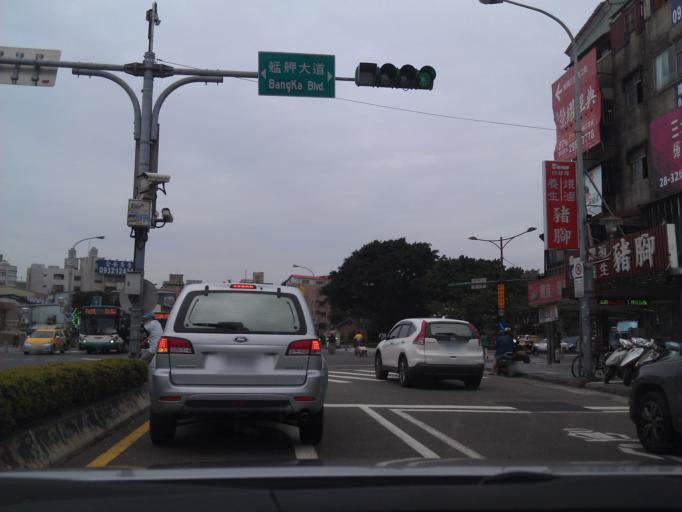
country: TW
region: Taipei
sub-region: Taipei
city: Banqiao
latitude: 25.0335
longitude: 121.4981
